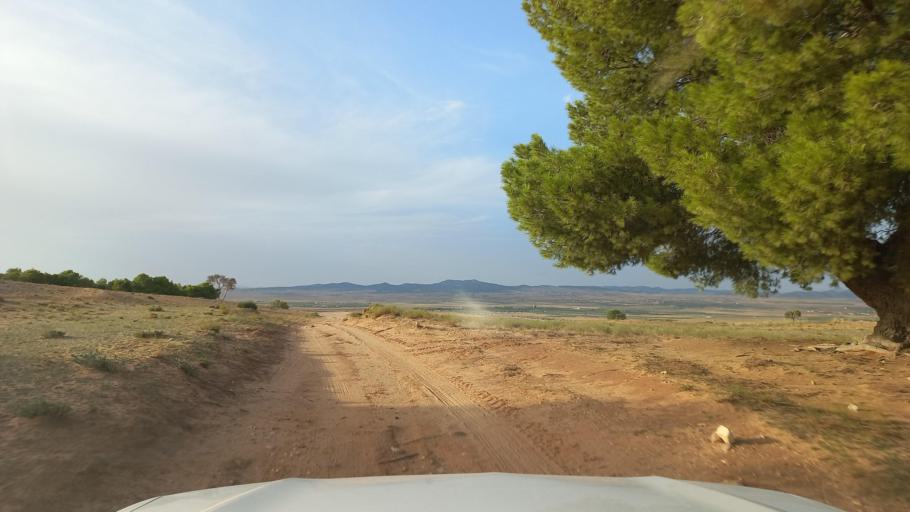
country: TN
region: Al Qasrayn
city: Sbiba
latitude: 35.4142
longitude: 8.8957
